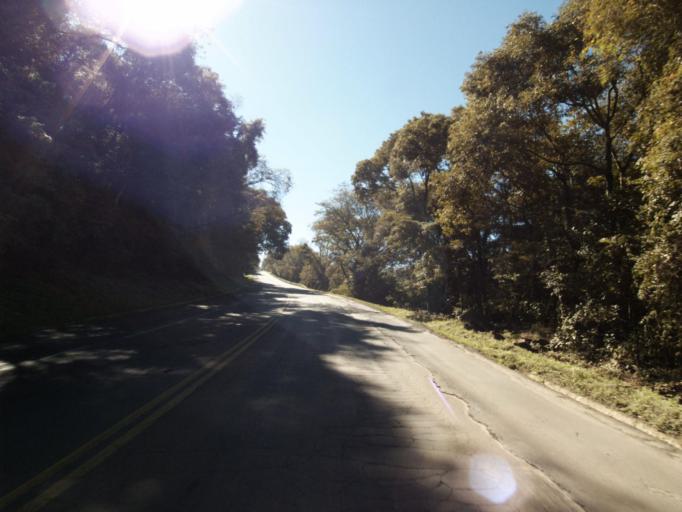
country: BR
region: Rio Grande do Sul
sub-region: Frederico Westphalen
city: Frederico Westphalen
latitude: -26.8031
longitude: -53.3122
